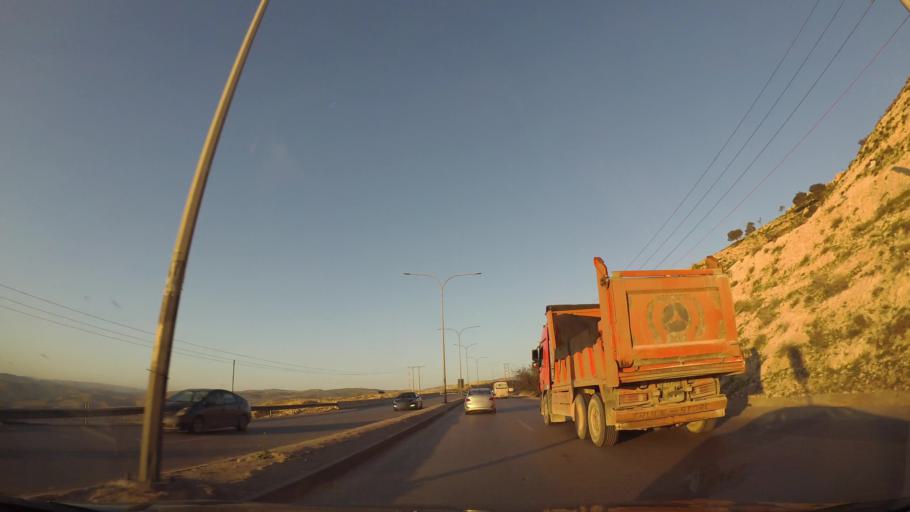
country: JO
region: Balqa
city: Yarqa
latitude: 31.8652
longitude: 35.7246
